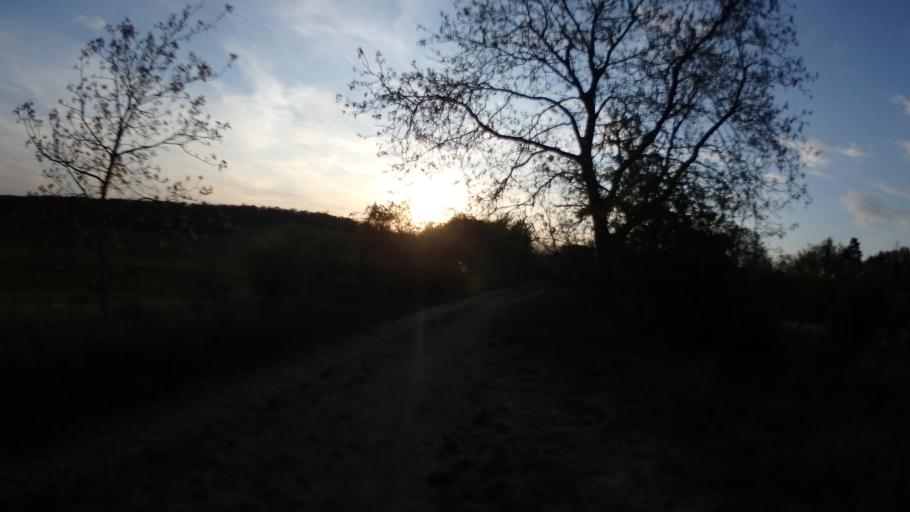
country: CZ
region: South Moravian
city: Ostopovice
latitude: 49.1503
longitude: 16.5429
